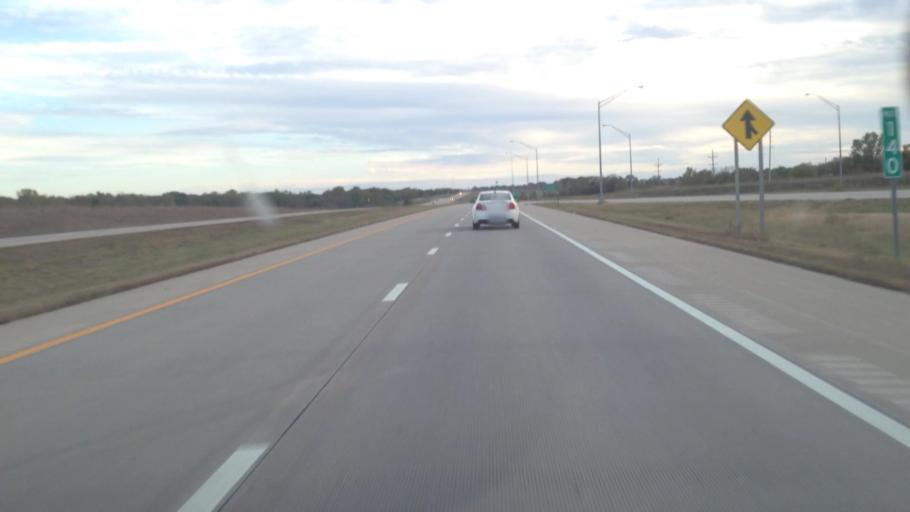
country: US
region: Kansas
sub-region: Douglas County
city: Baldwin City
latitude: 38.7199
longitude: -95.2685
